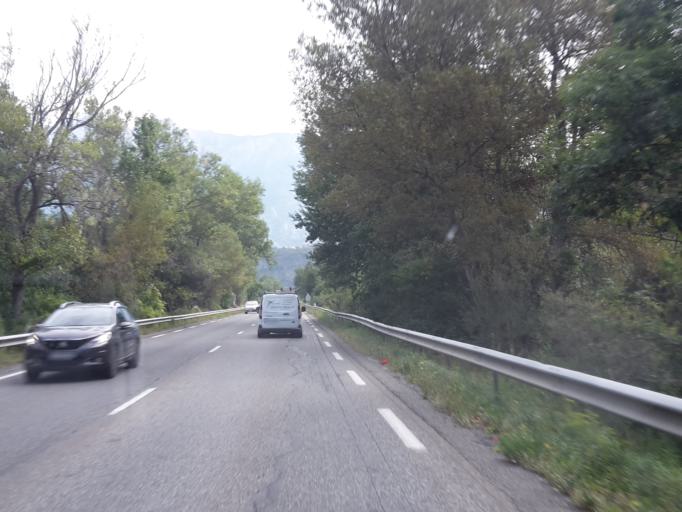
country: FR
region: Provence-Alpes-Cote d'Azur
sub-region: Departement des Hautes-Alpes
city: Guillestre
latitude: 44.6561
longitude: 6.5959
